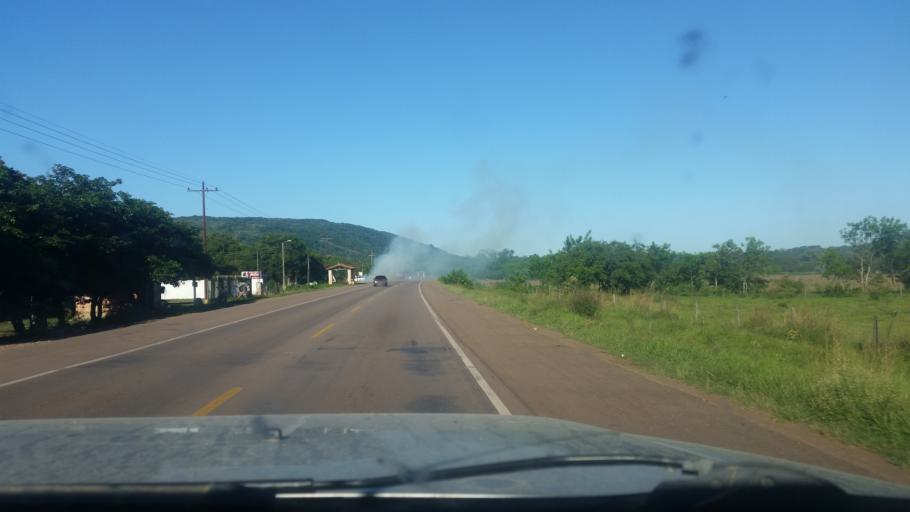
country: PY
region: Paraguari
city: Sapucai
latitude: -25.6511
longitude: -56.9917
